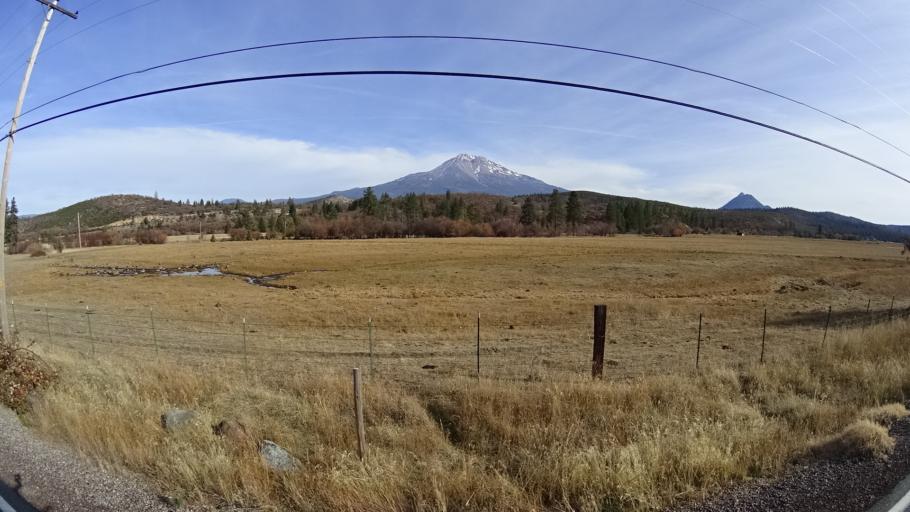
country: US
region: California
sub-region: Siskiyou County
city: Weed
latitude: 41.4300
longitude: -122.4372
